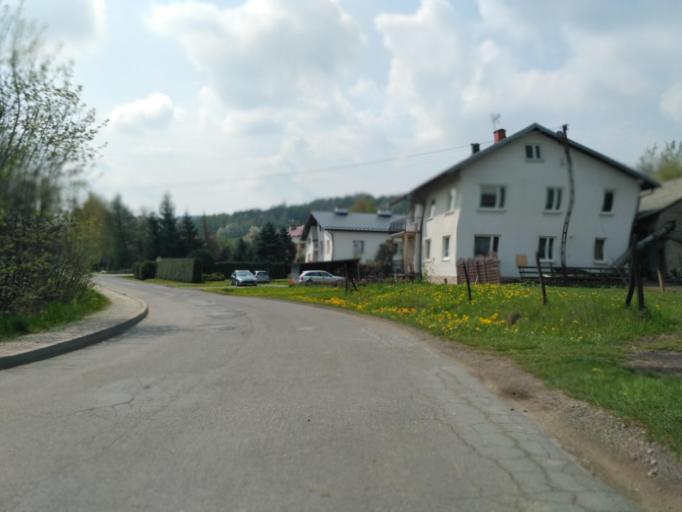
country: PL
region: Subcarpathian Voivodeship
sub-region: Powiat krosnienski
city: Iwonicz-Zdroj
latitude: 49.5848
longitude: 21.7508
